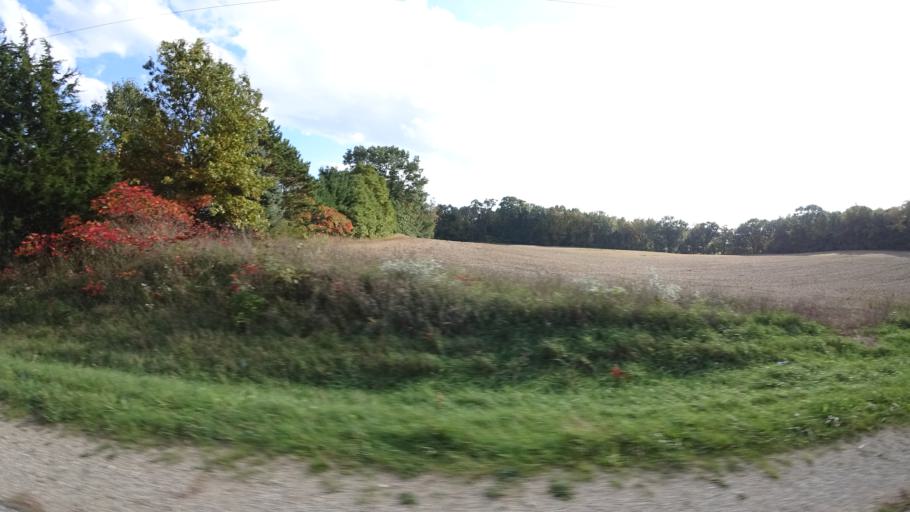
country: US
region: Michigan
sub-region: Saint Joseph County
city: Centreville
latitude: 41.8537
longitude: -85.4832
